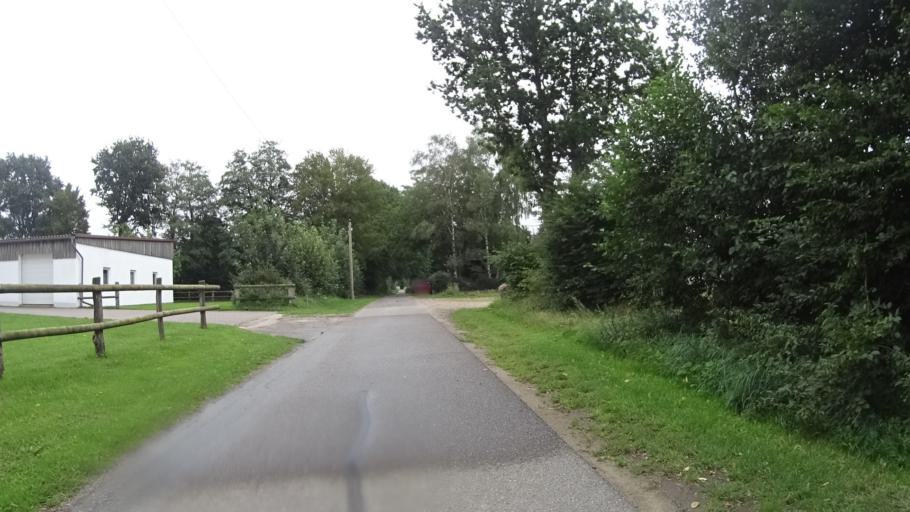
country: DE
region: Schleswig-Holstein
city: Lasbek
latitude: 53.7314
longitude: 10.3787
